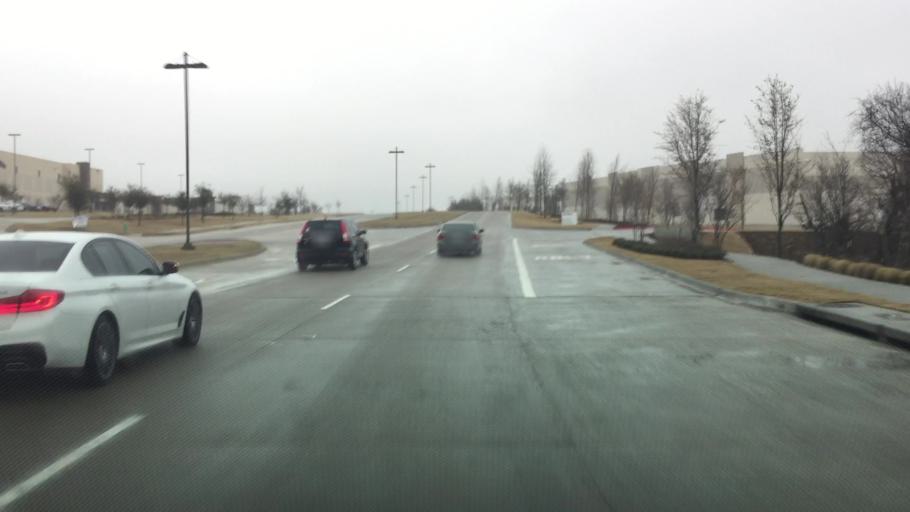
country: US
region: Texas
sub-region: Denton County
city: Flower Mound
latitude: 32.9947
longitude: -97.0577
